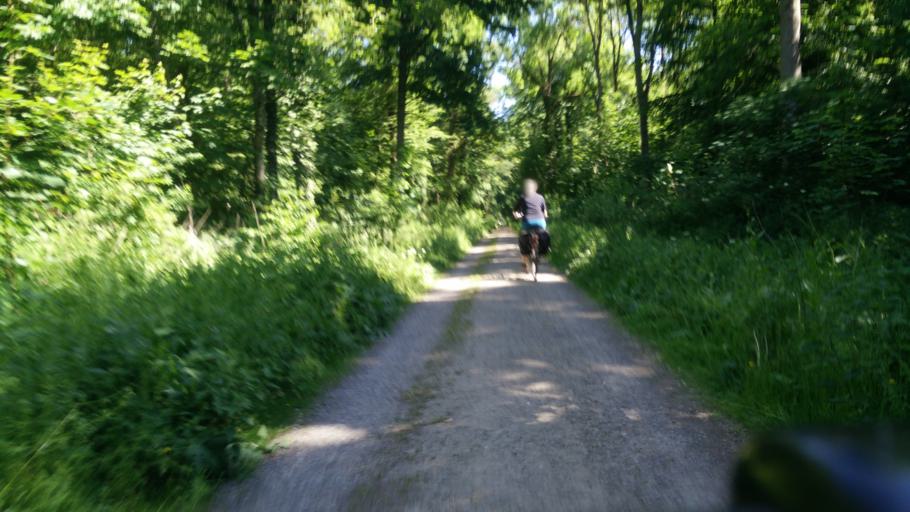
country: DE
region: Lower Saxony
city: Haste
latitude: 52.3811
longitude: 9.3850
